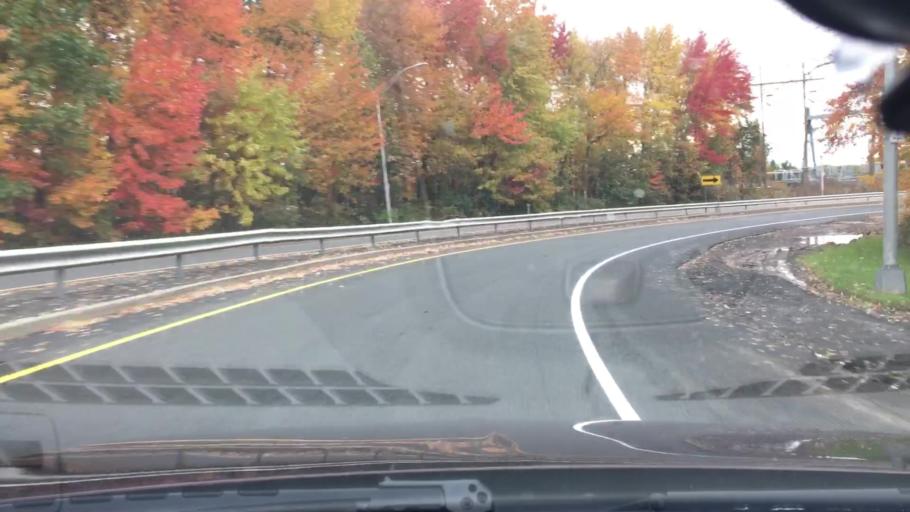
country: US
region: Connecticut
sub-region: New Haven County
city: Cheshire Village
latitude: 41.5746
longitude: -72.9033
